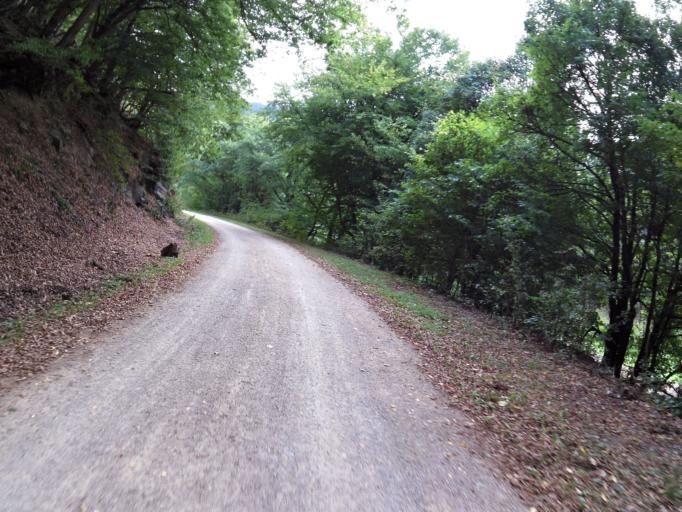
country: DE
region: North Rhine-Westphalia
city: Heimbach
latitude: 50.5829
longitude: 6.4629
